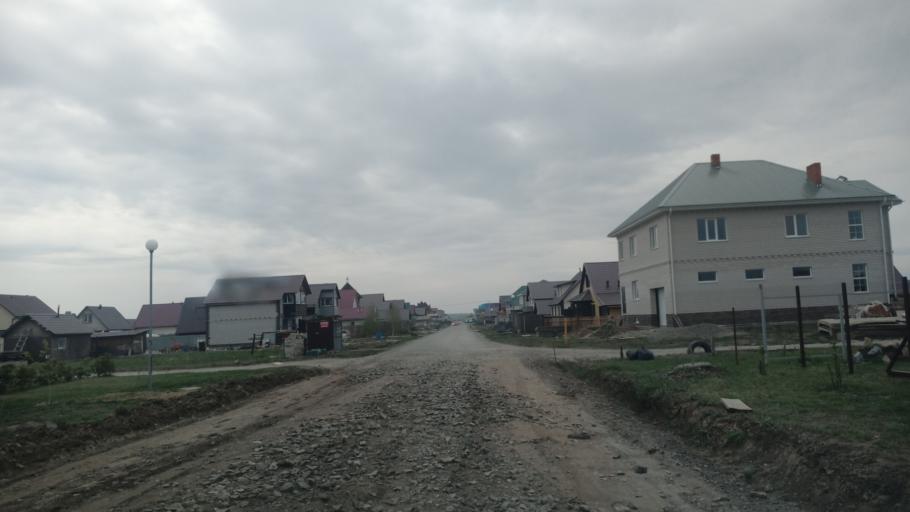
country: RU
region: Altai Krai
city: Yuzhnyy
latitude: 53.2254
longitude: 83.6908
